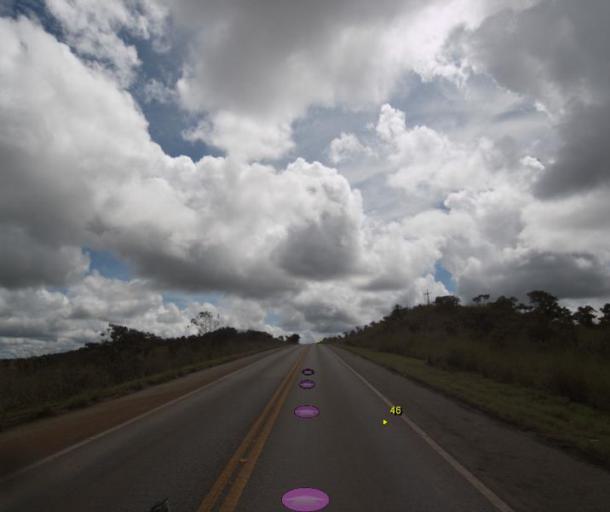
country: BR
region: Goias
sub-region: Pirenopolis
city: Pirenopolis
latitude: -15.7571
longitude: -48.5818
